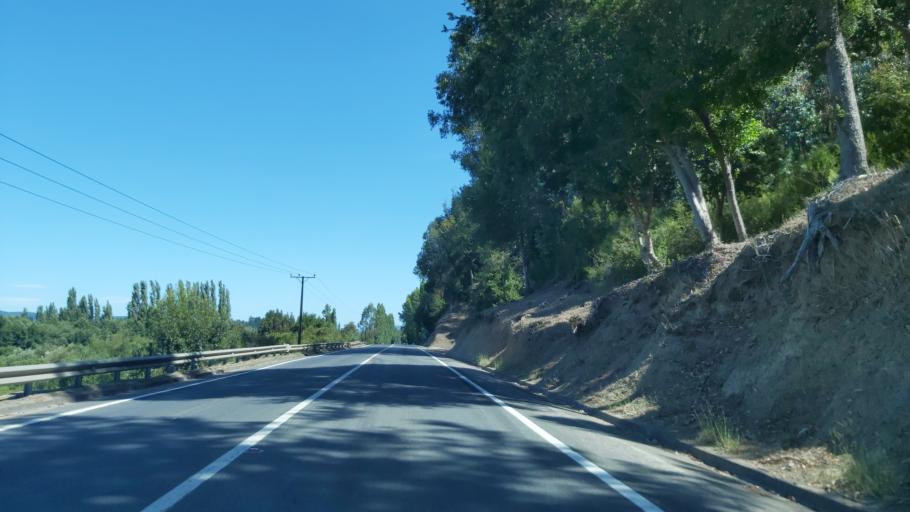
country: CL
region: Biobio
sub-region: Provincia de Concepcion
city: Lota
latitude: -37.1402
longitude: -72.9782
